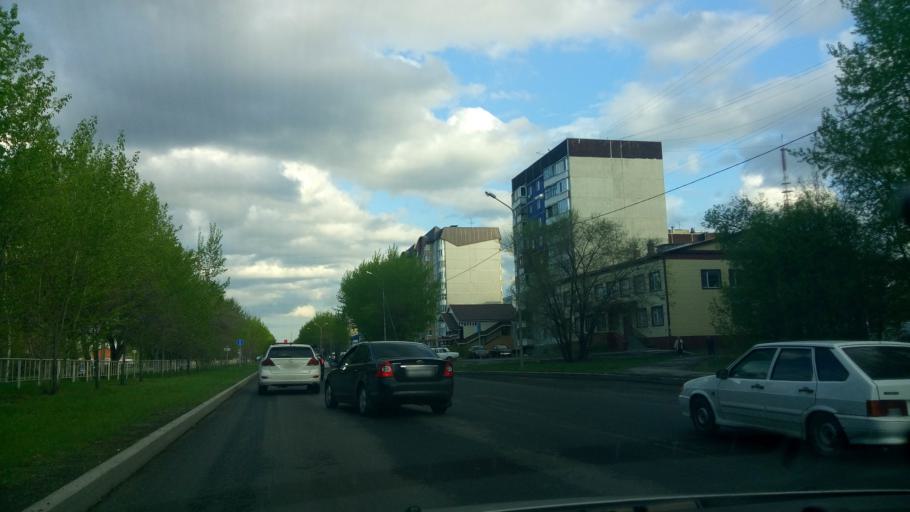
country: RU
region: Tjumen
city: Tyumen
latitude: 57.1381
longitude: 65.5957
